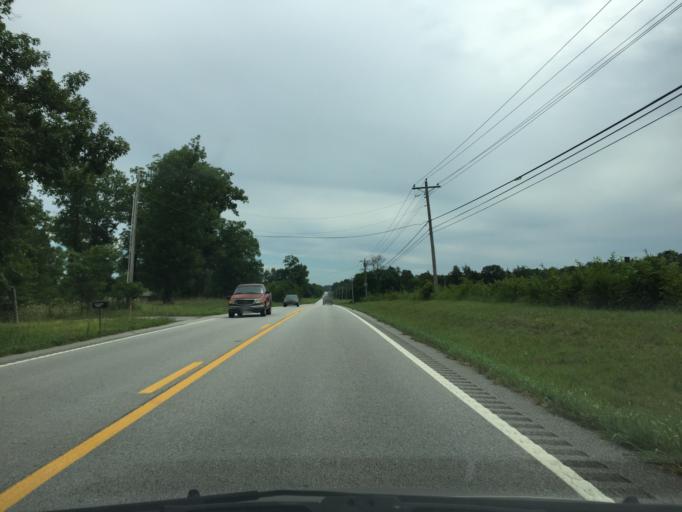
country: US
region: Tennessee
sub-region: Bradley County
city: Hopewell
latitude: 35.2869
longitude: -84.9715
